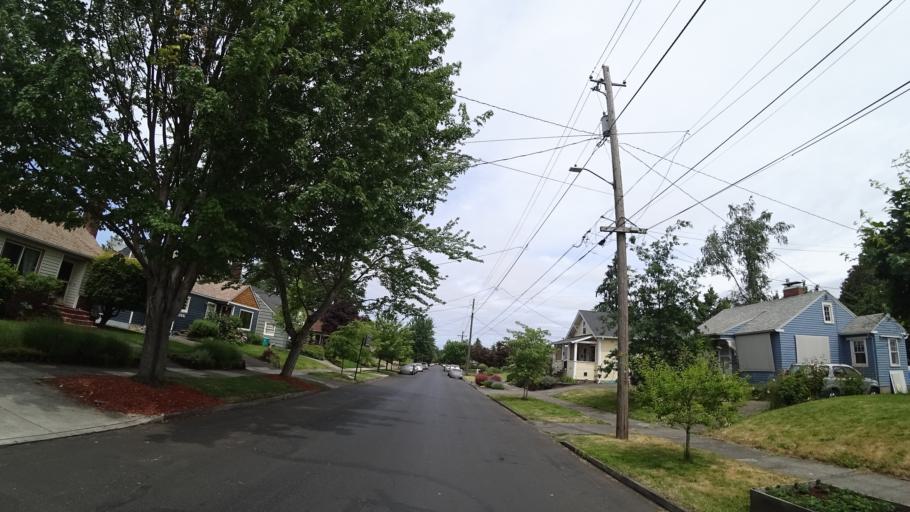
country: US
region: Oregon
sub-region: Multnomah County
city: Portland
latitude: 45.5616
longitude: -122.6287
